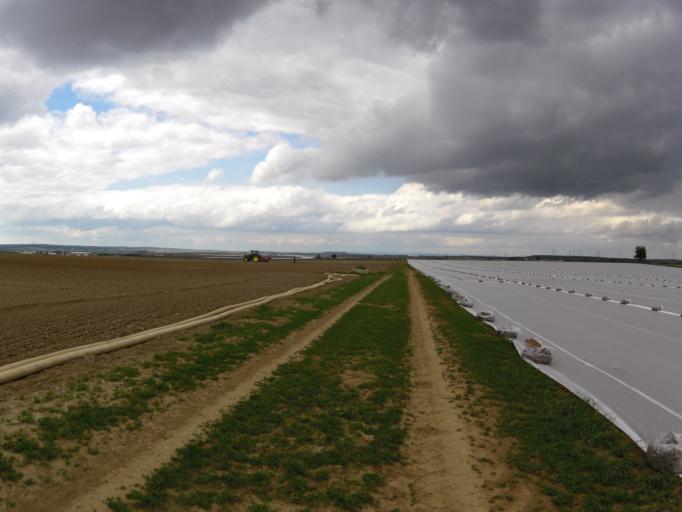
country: DE
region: Bavaria
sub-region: Regierungsbezirk Unterfranken
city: Oberpleichfeld
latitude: 49.8540
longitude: 10.0874
